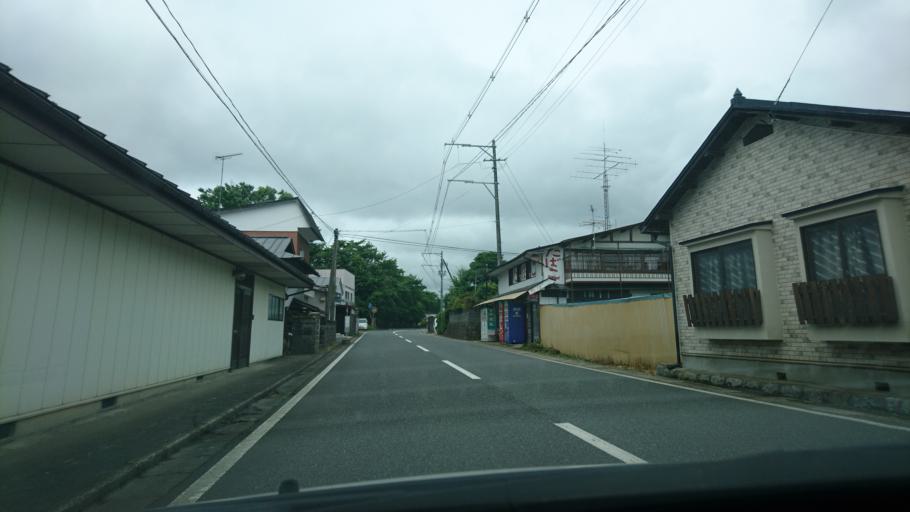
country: JP
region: Iwate
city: Ichinoseki
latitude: 38.9429
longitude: 141.0534
